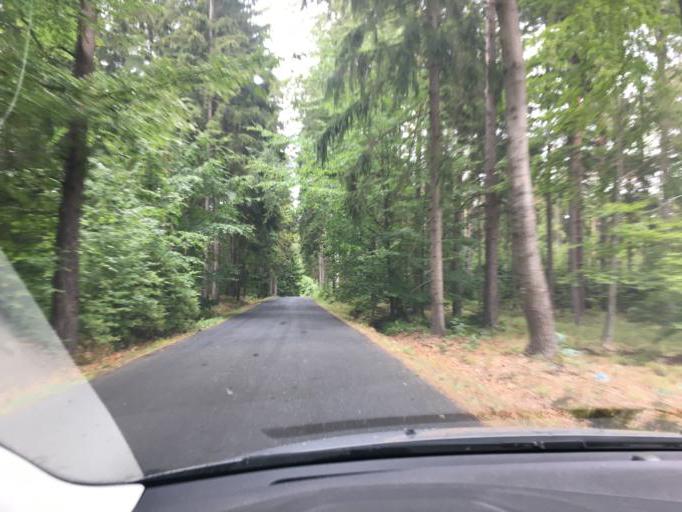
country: CZ
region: Ustecky
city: Benesov nad Ploucnici
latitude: 50.8222
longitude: 14.3134
